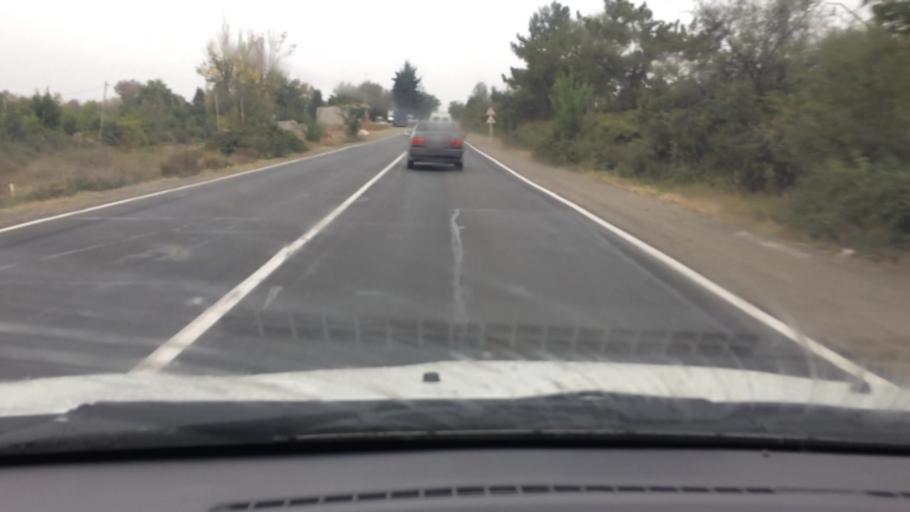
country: GE
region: Kvemo Kartli
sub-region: Marneuli
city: Marneuli
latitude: 41.4108
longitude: 44.8309
